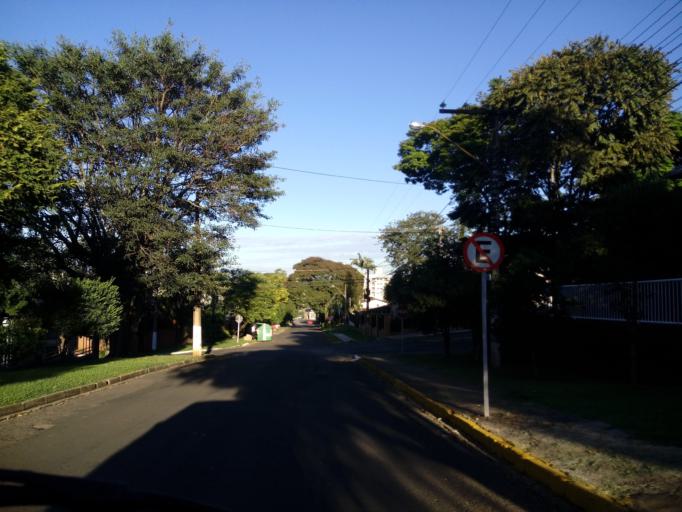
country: BR
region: Santa Catarina
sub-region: Chapeco
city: Chapeco
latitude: -27.1143
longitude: -52.6134
